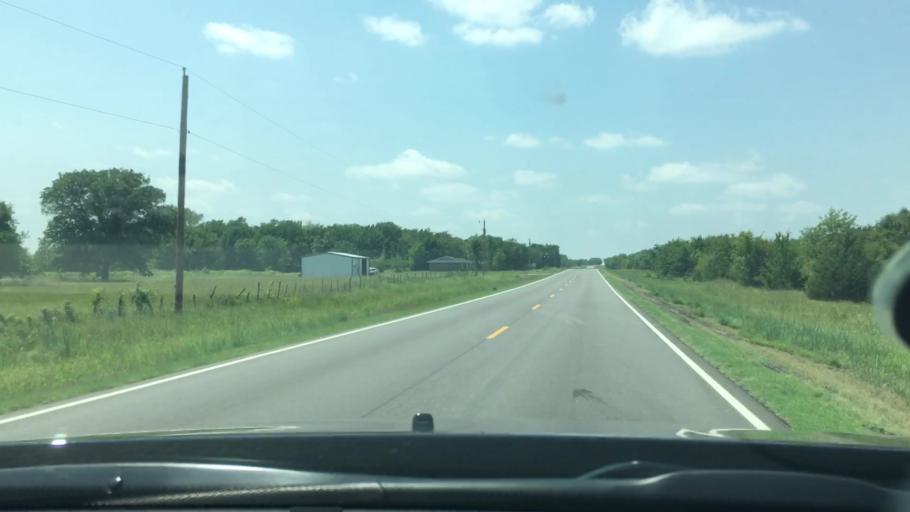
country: US
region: Oklahoma
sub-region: Atoka County
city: Atoka
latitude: 34.3747
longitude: -96.1819
